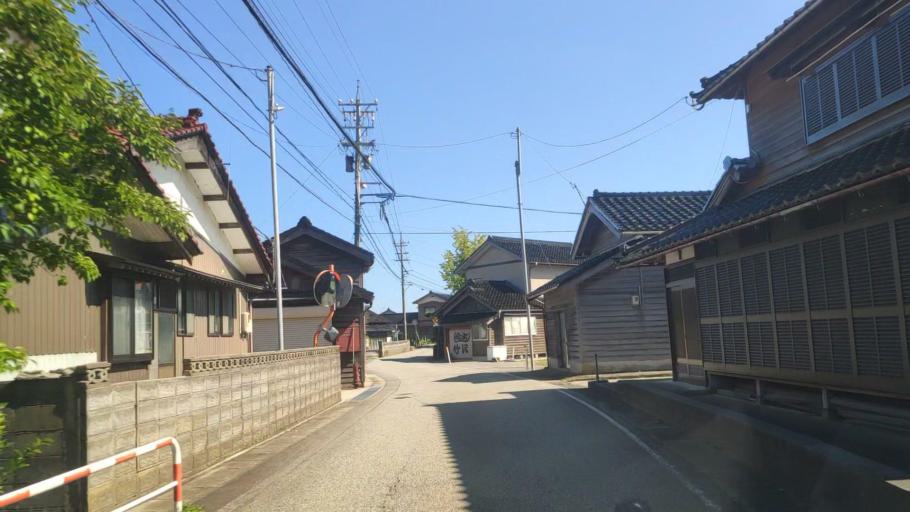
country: JP
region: Toyama
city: Nyuzen
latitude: 37.5051
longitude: 137.3475
